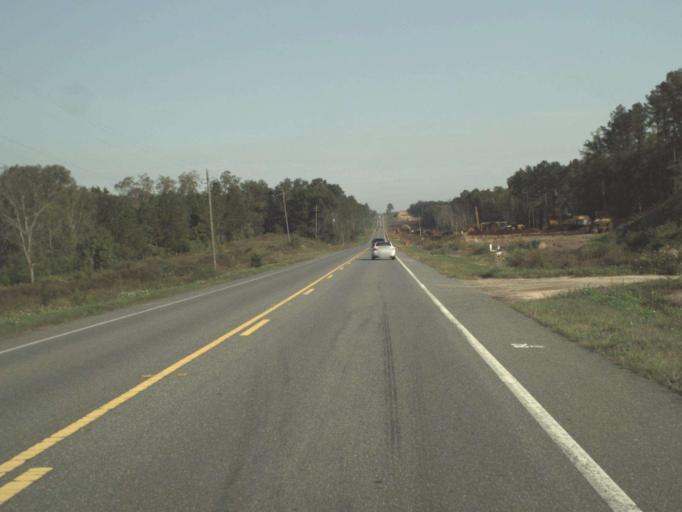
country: US
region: Florida
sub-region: Holmes County
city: Bonifay
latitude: 30.7072
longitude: -85.6859
